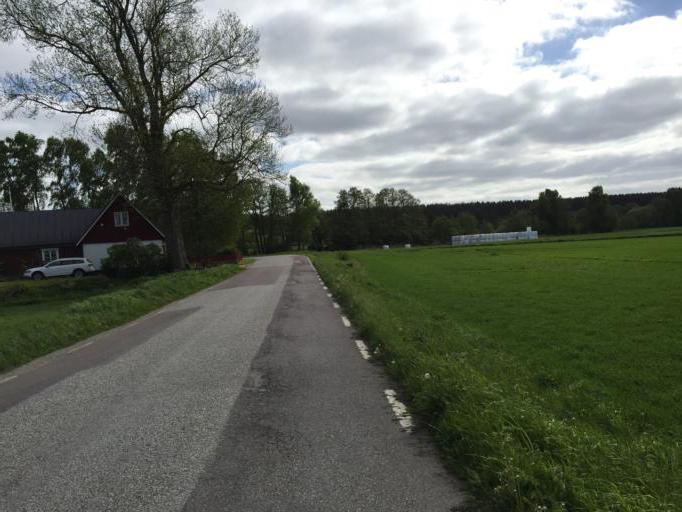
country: SE
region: Skane
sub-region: Sjobo Kommun
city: Blentarp
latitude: 55.6640
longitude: 13.6183
